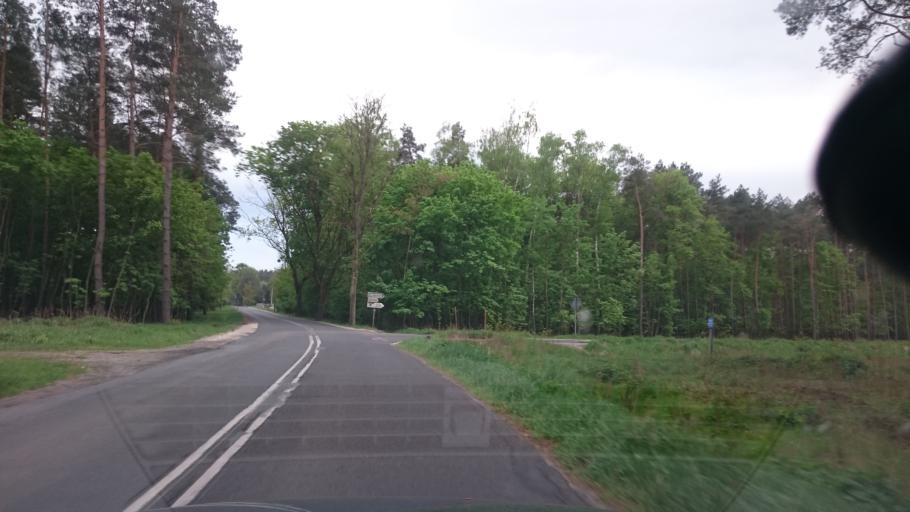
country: PL
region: Kujawsko-Pomorskie
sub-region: Grudziadz
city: Grudziadz
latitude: 53.4422
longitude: 18.7746
